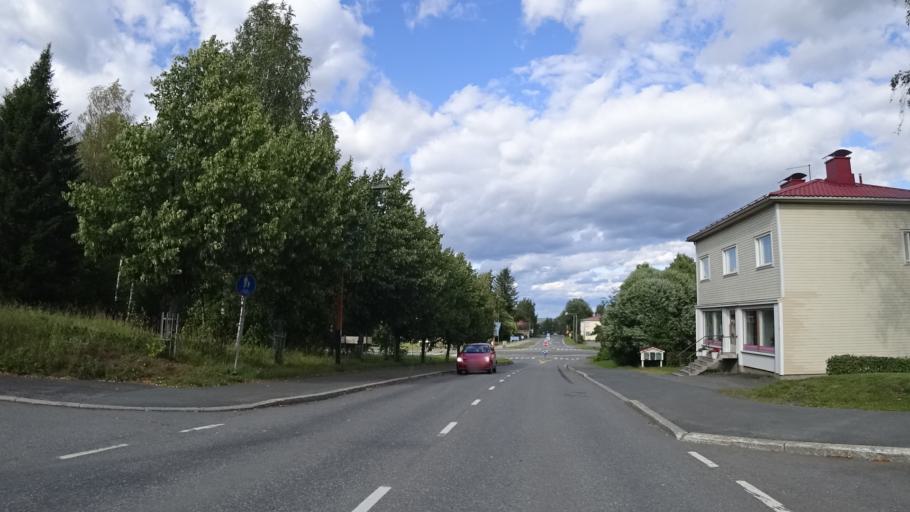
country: FI
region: North Karelia
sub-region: Keski-Karjala
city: Tohmajaervi
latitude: 62.2254
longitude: 30.3311
